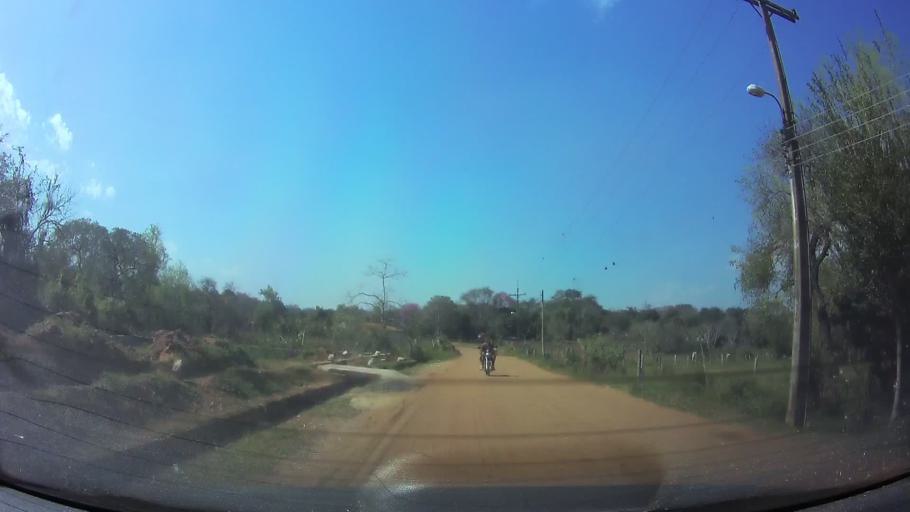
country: PY
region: Central
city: Limpio
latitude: -25.2329
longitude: -57.4451
